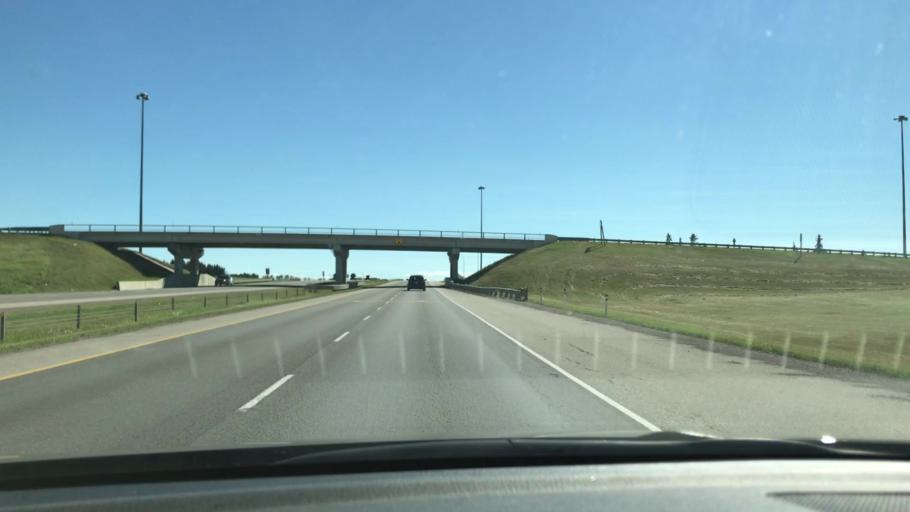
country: CA
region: Alberta
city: Penhold
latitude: 52.0272
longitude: -113.9300
